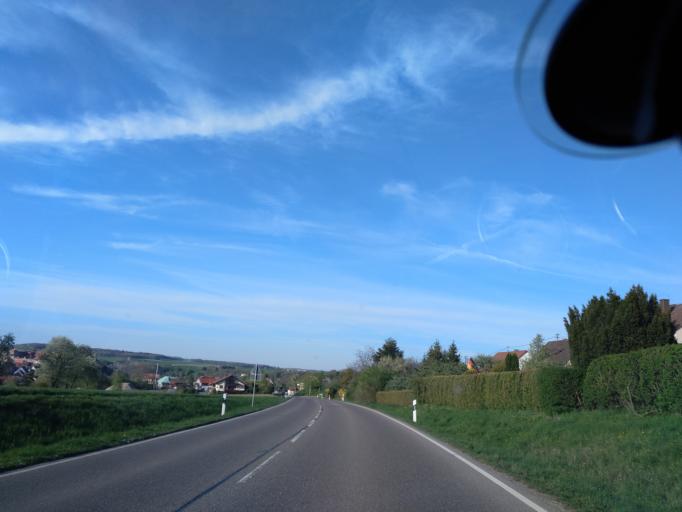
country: DE
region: Baden-Wuerttemberg
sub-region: Regierungsbezirk Stuttgart
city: Kirchberg an der Jagst
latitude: 49.1978
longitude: 9.9794
